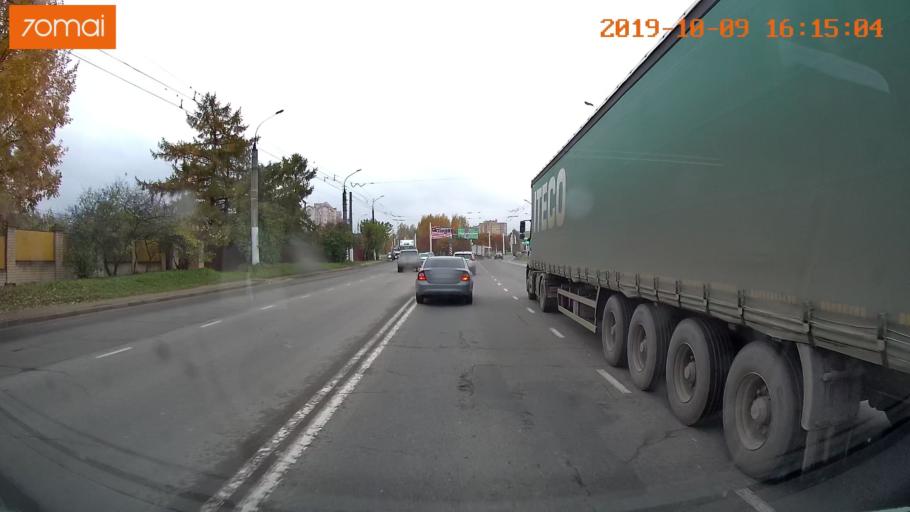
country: RU
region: Kostroma
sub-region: Kostromskoy Rayon
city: Kostroma
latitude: 57.7416
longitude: 40.9194
